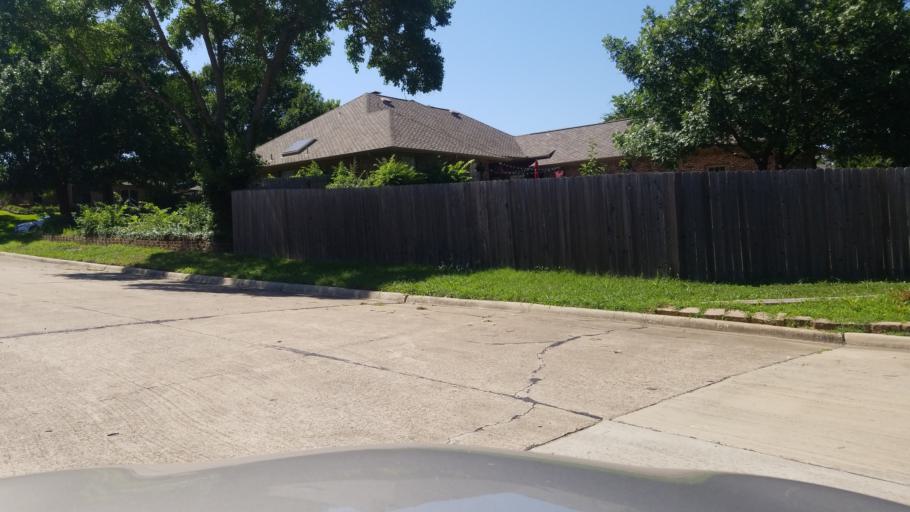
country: US
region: Texas
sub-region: Dallas County
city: Grand Prairie
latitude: 32.6843
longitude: -96.9963
